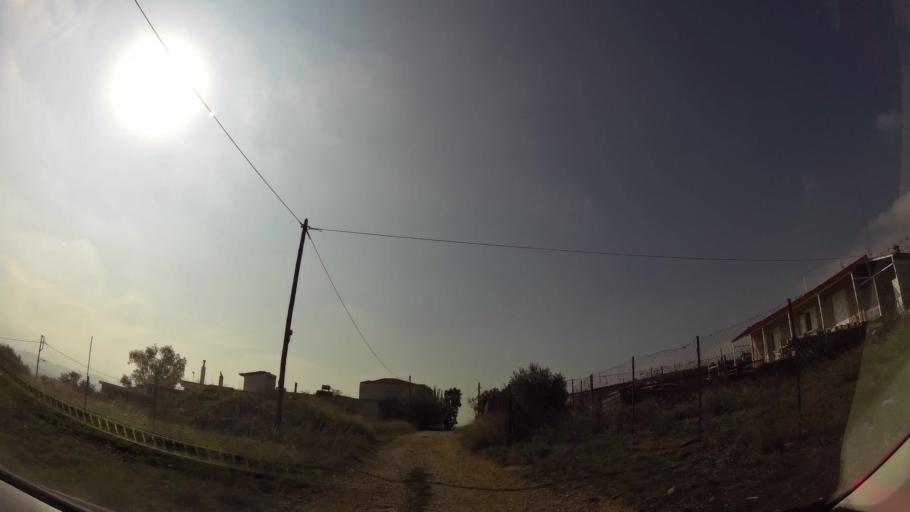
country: GR
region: Attica
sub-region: Nomarchia Dytikis Attikis
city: Zefyri
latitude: 38.0604
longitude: 23.7264
